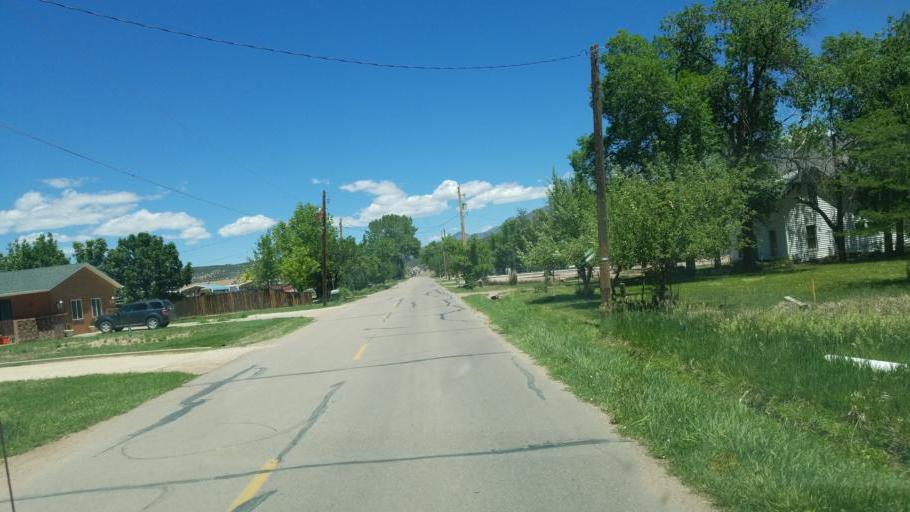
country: US
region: Colorado
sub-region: Fremont County
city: Canon City
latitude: 38.4807
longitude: -105.2086
